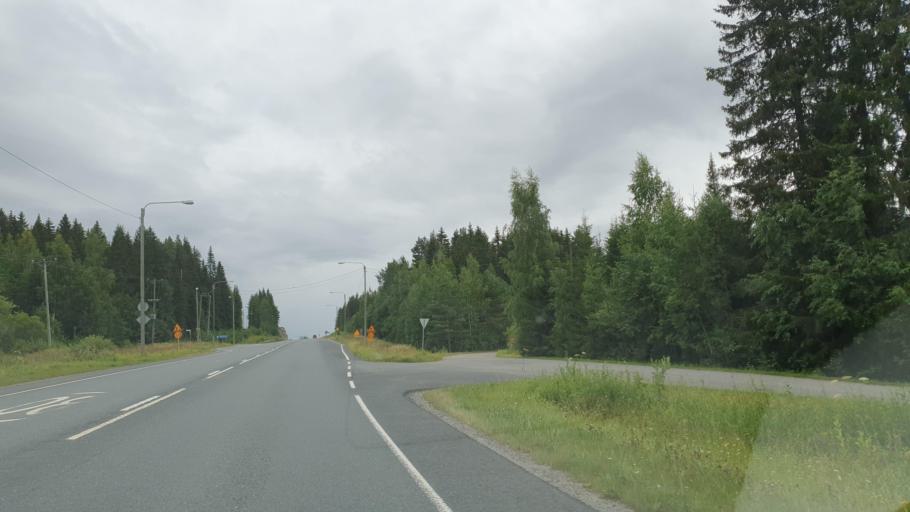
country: FI
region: Northern Savo
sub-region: Ylae-Savo
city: Lapinlahti
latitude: 63.3090
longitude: 27.4488
